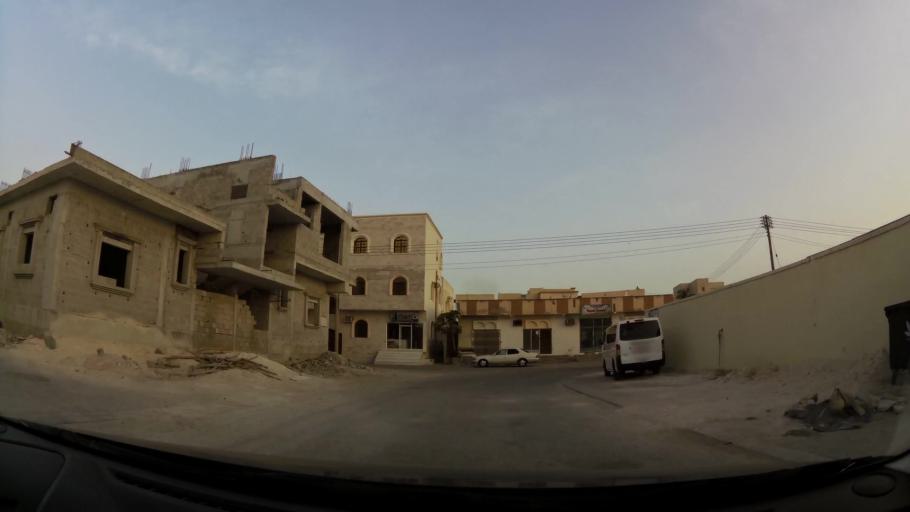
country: OM
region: Zufar
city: Salalah
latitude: 17.0206
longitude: 54.1231
